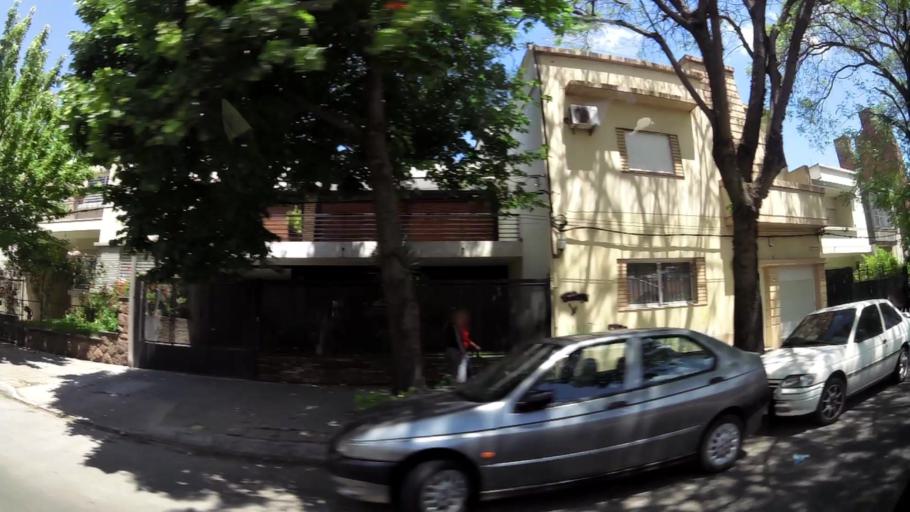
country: UY
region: Montevideo
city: Montevideo
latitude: -34.8709
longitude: -56.2043
